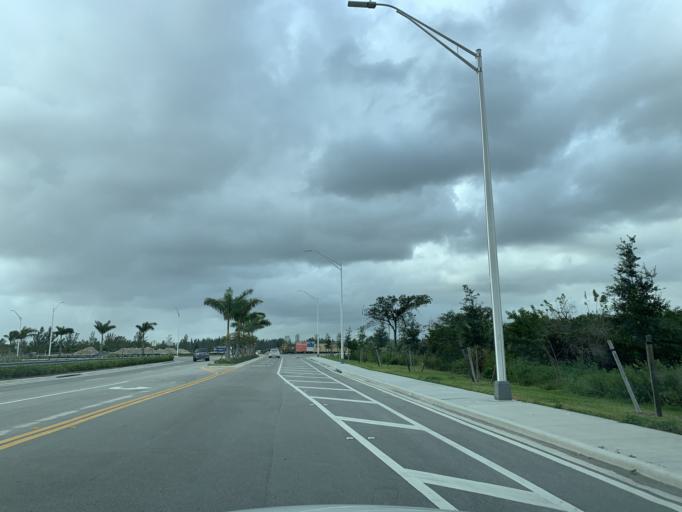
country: US
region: Florida
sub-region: Miami-Dade County
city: Sweetwater
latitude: 25.7863
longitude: -80.3892
